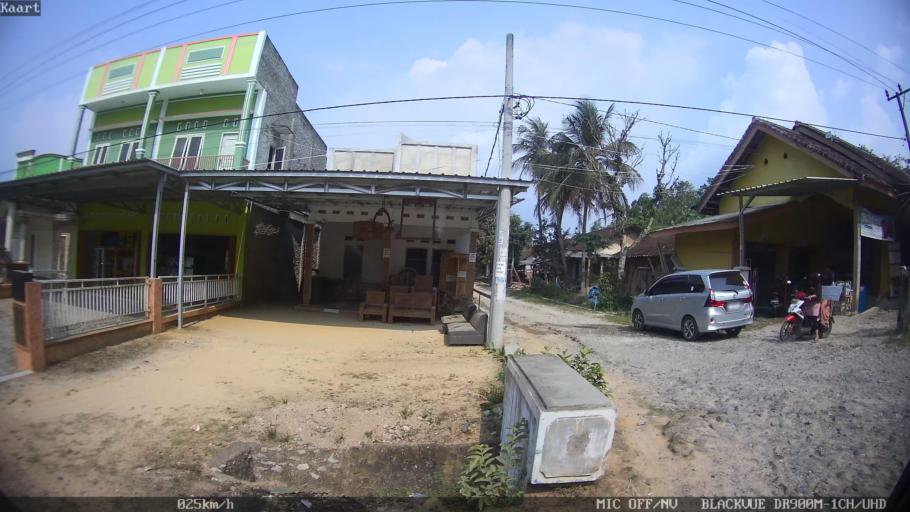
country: ID
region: Lampung
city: Pringsewu
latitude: -5.4041
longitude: 104.9929
